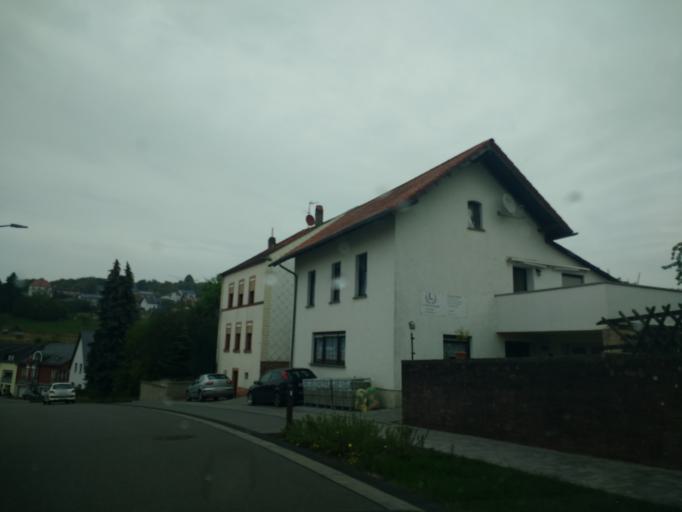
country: DE
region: Rheinland-Pfalz
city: Freudenburg
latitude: 49.5394
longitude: 6.5363
